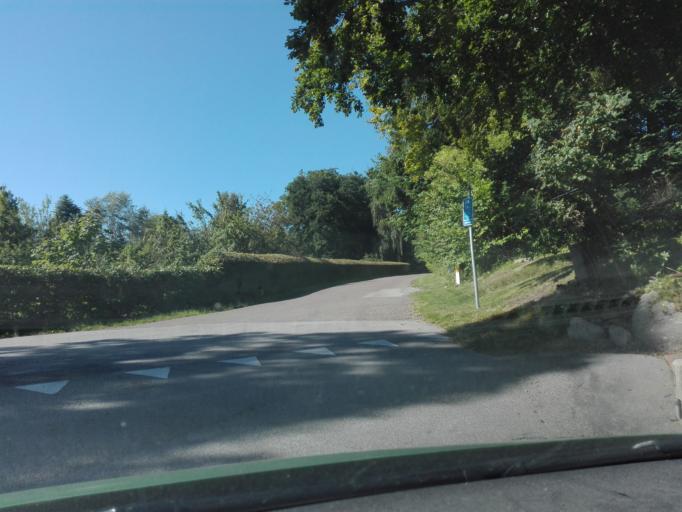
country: DK
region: North Denmark
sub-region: Mariagerfjord Kommune
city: Mariager
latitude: 56.6730
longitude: 9.9699
